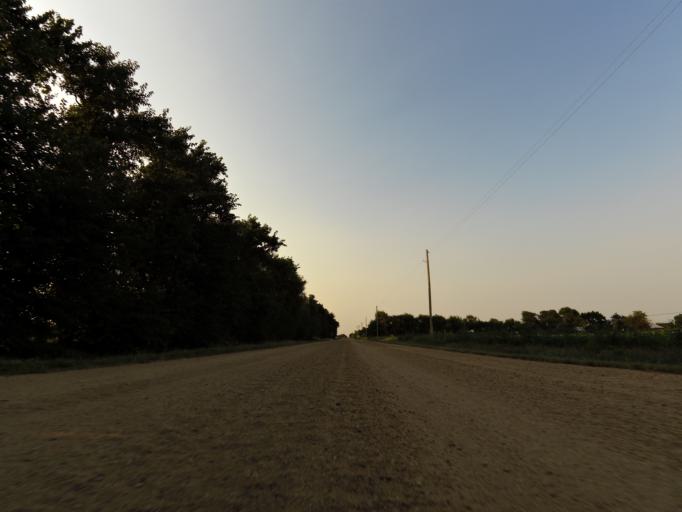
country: US
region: Kansas
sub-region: Reno County
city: South Hutchinson
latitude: 37.9966
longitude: -97.9956
